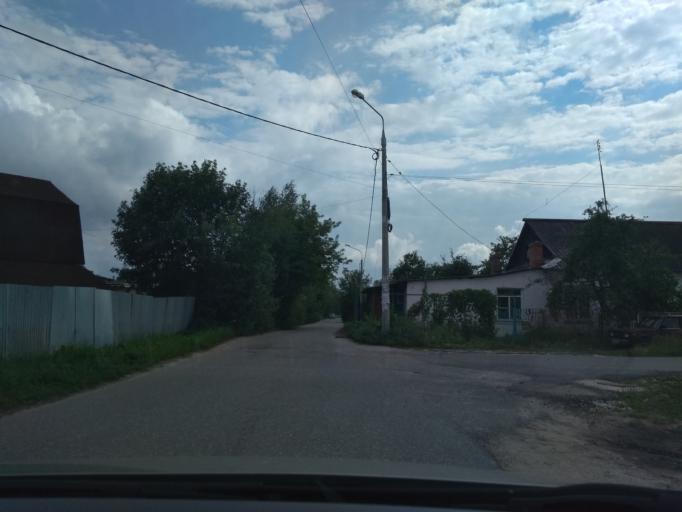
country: RU
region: Moskovskaya
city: Orekhovo-Zuyevo
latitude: 55.7882
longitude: 38.9272
